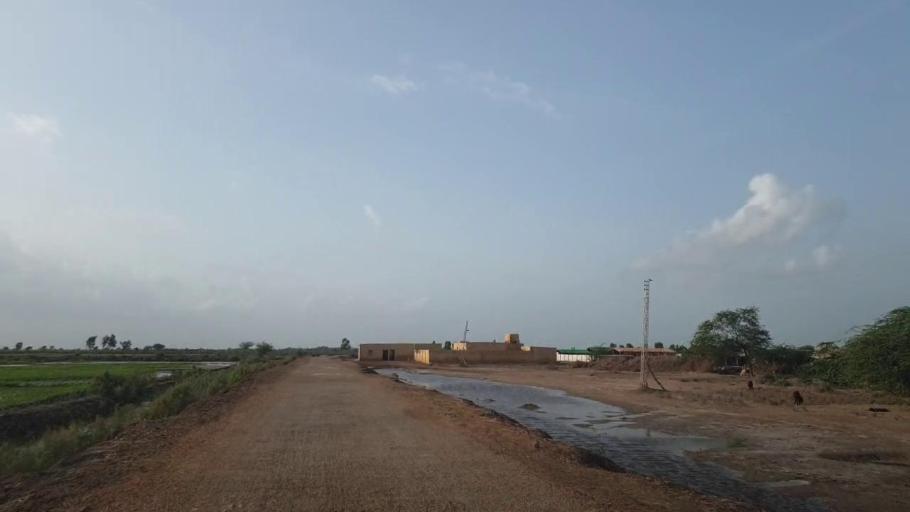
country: PK
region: Sindh
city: Tando Bago
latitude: 24.6609
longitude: 69.1120
